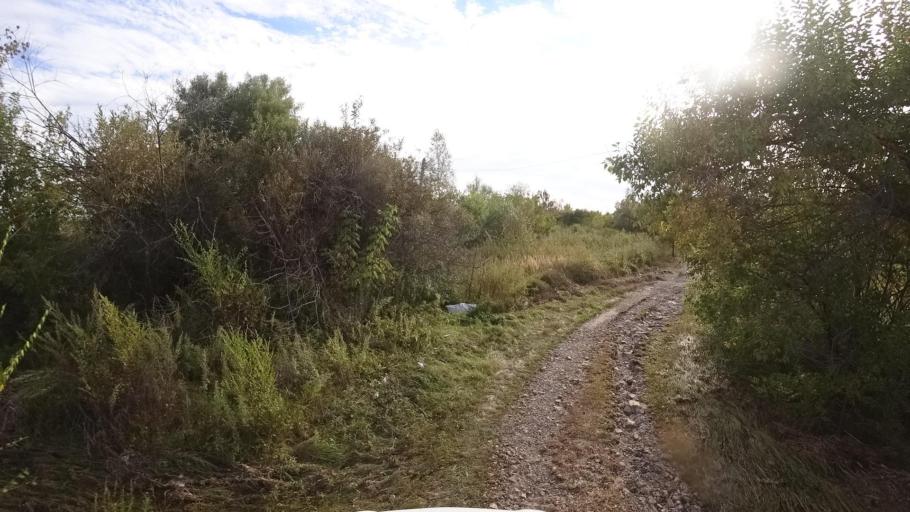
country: RU
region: Primorskiy
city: Dostoyevka
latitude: 44.2936
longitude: 133.4261
